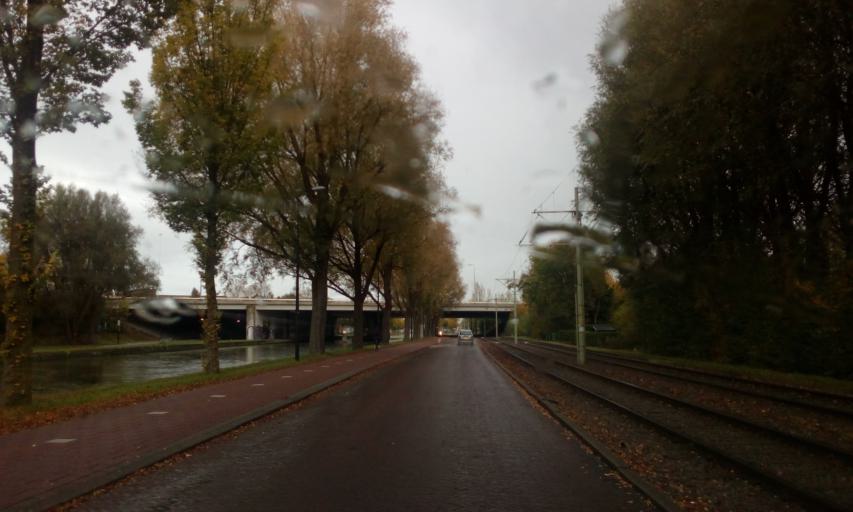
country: NL
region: South Holland
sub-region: Gemeente Rijswijk
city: Rijswijk
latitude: 52.0393
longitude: 4.3450
